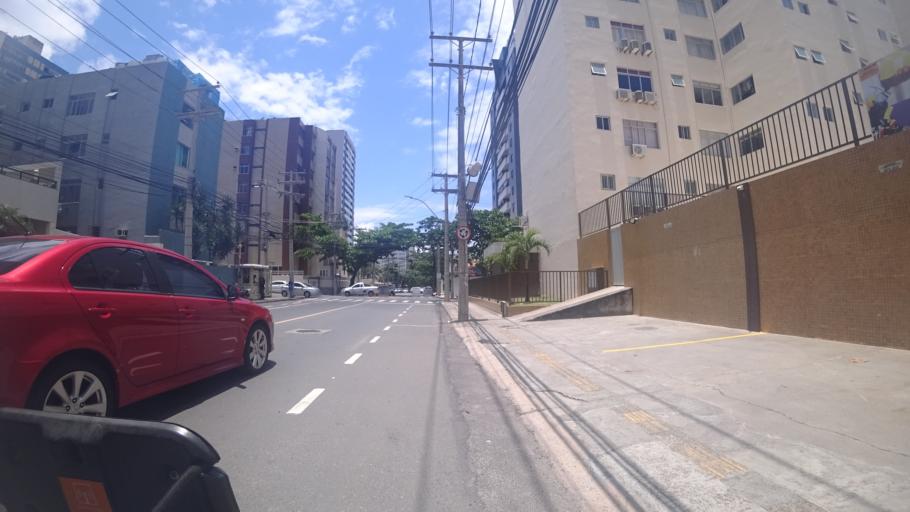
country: BR
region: Bahia
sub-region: Salvador
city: Salvador
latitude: -13.0072
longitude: -38.4641
